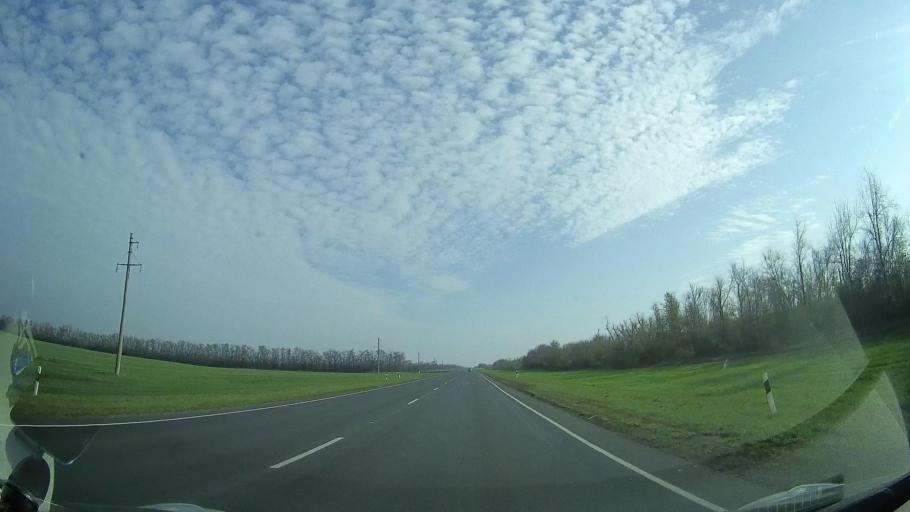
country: RU
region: Rostov
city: Gigant
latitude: 46.5274
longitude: 41.2125
